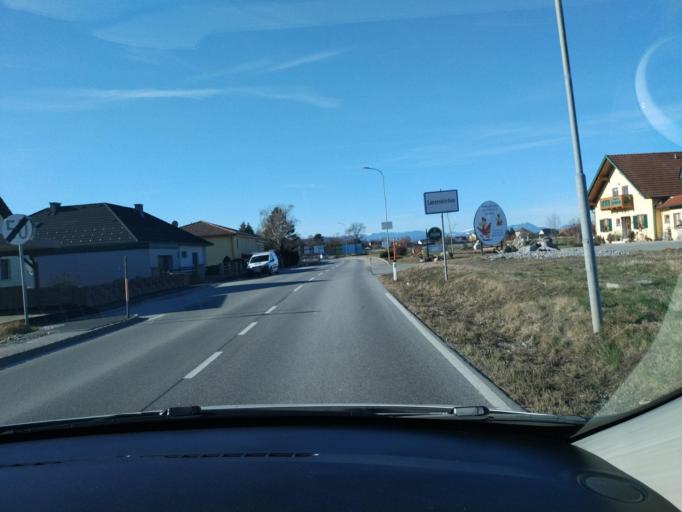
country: AT
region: Lower Austria
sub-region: Politischer Bezirk Wiener Neustadt
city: Lanzenkirchen
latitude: 47.7528
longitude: 16.2515
